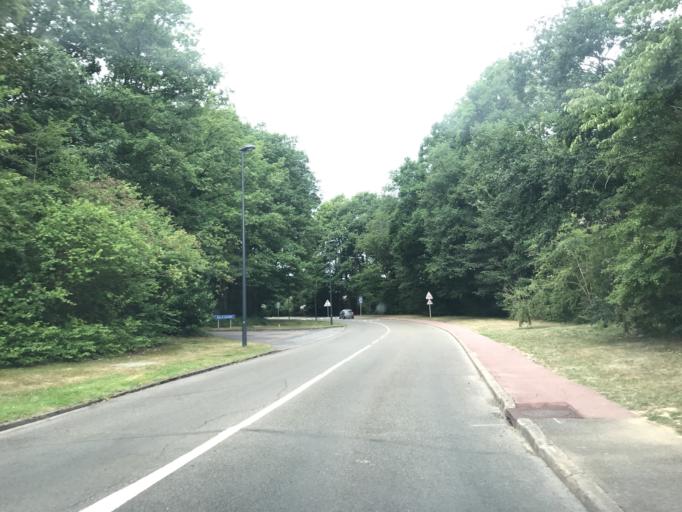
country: FR
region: Ile-de-France
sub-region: Departement des Yvelines
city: Maurepas
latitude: 48.7753
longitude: 1.9392
